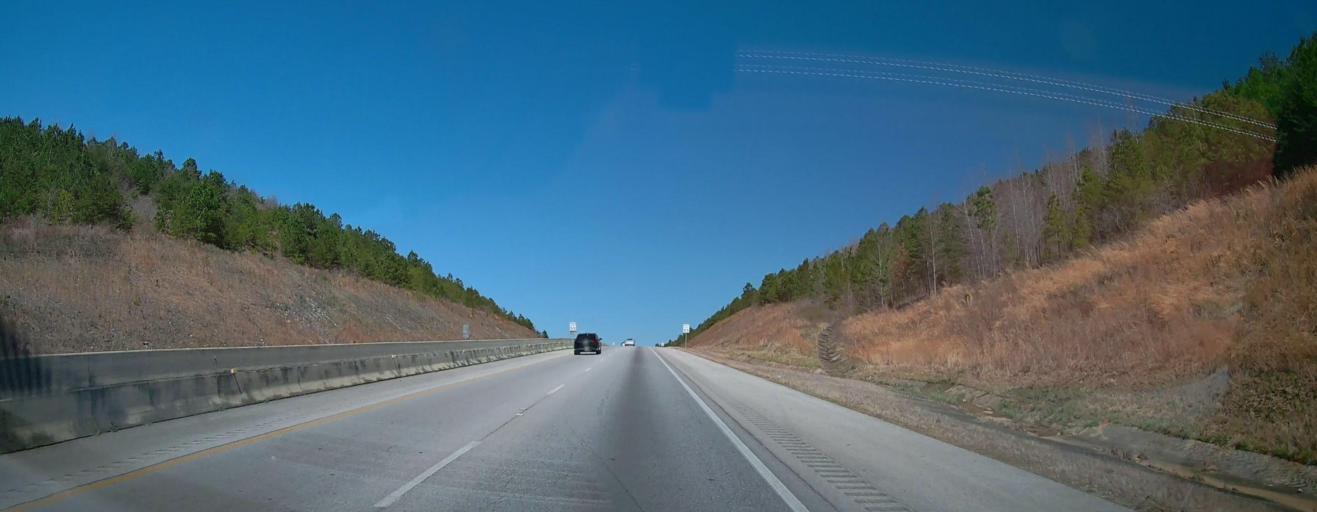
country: US
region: Alabama
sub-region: Calhoun County
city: Anniston
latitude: 33.6631
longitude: -85.7860
